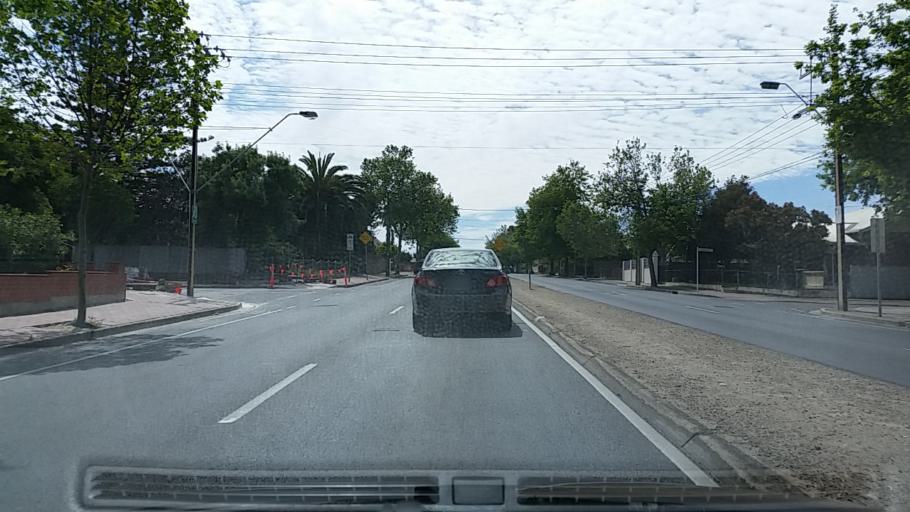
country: AU
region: South Australia
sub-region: Prospect
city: Prospect
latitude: -34.8739
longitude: 138.5977
